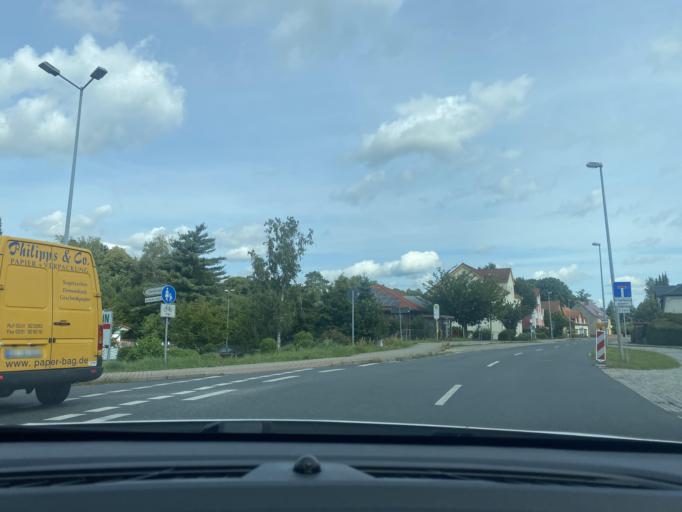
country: DE
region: Saxony
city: Krauschwitz
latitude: 51.5159
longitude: 14.7181
